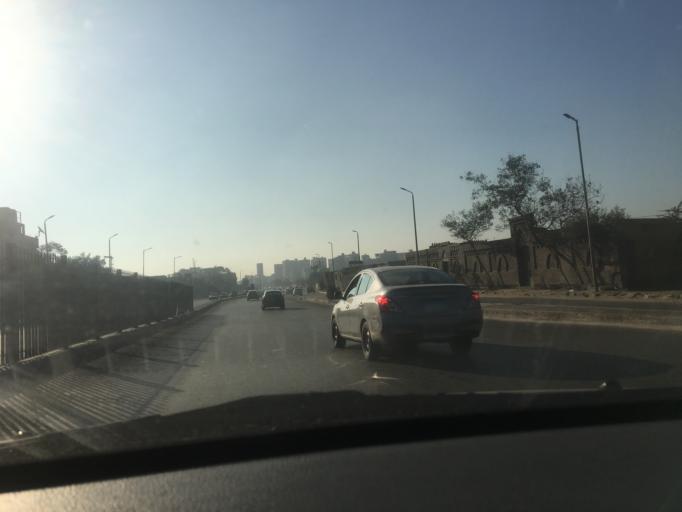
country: EG
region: Muhafazat al Qahirah
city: Cairo
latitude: 30.0204
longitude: 31.2640
